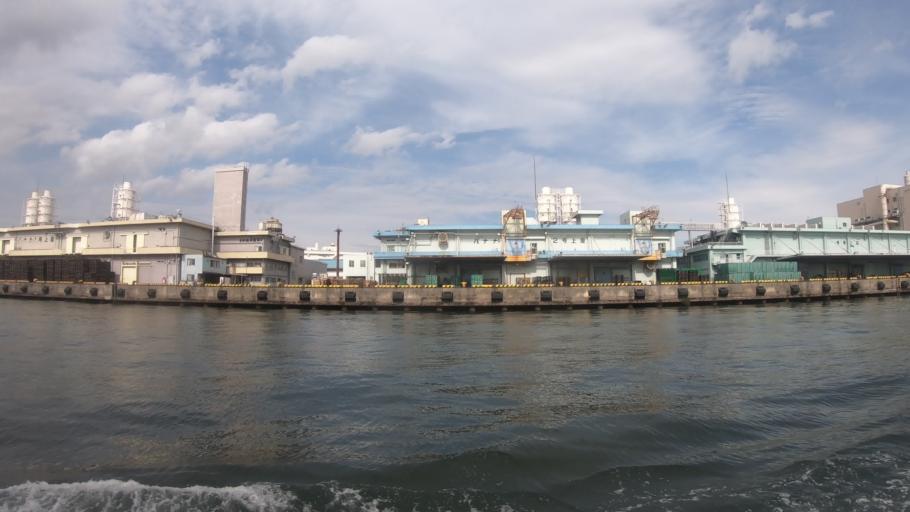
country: JP
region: Kanagawa
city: Yokohama
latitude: 35.4757
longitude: 139.6496
